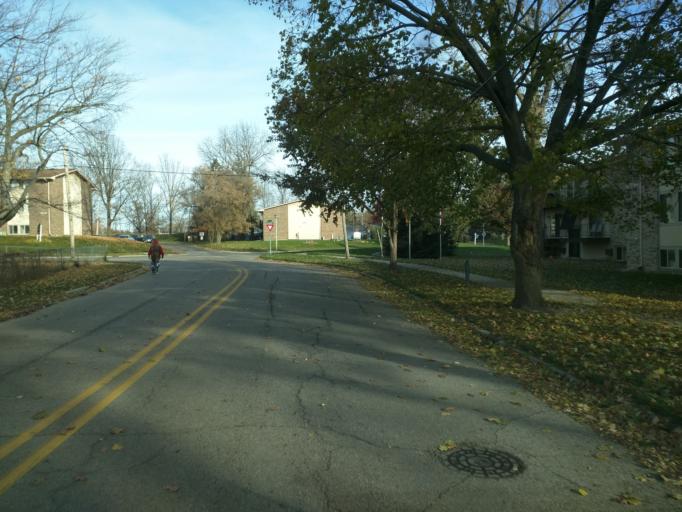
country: US
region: Michigan
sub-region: Ingham County
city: Holt
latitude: 42.6760
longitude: -84.5456
